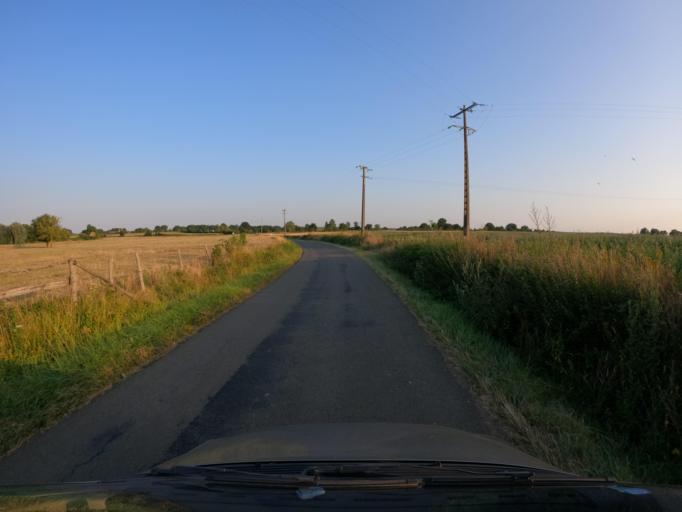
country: FR
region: Pays de la Loire
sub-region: Departement de la Sarthe
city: Brulon
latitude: 47.9176
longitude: -0.2293
